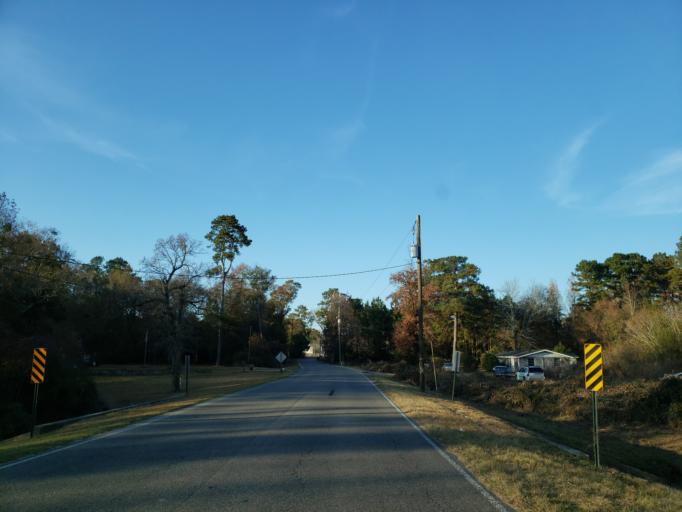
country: US
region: Mississippi
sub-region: Lamar County
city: Arnold Line
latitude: 31.3426
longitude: -89.3597
